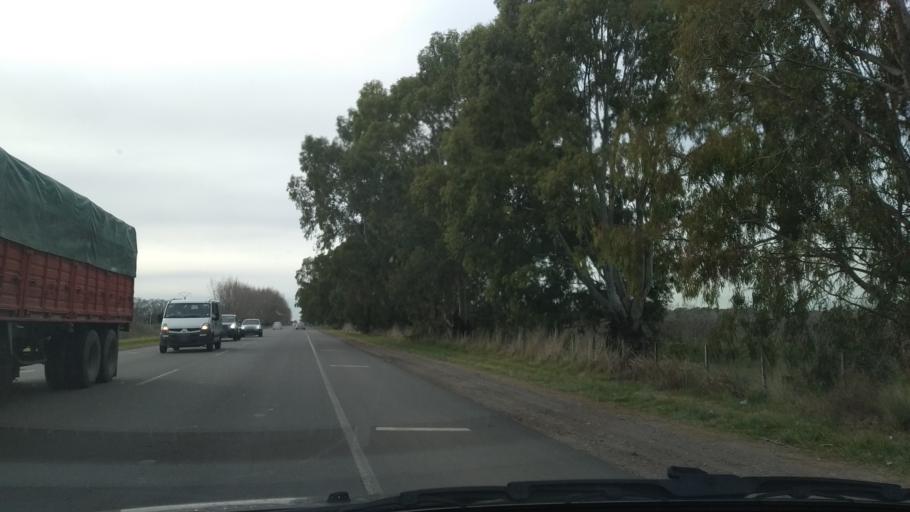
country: AR
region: Buenos Aires
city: Olavarria
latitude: -36.9714
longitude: -60.2739
